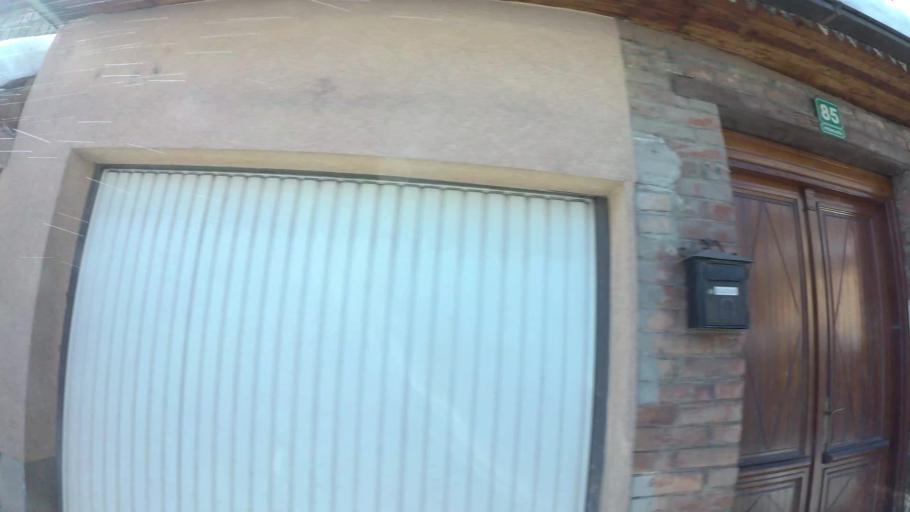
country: BA
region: Federation of Bosnia and Herzegovina
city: Kobilja Glava
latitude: 43.8670
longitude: 18.4286
